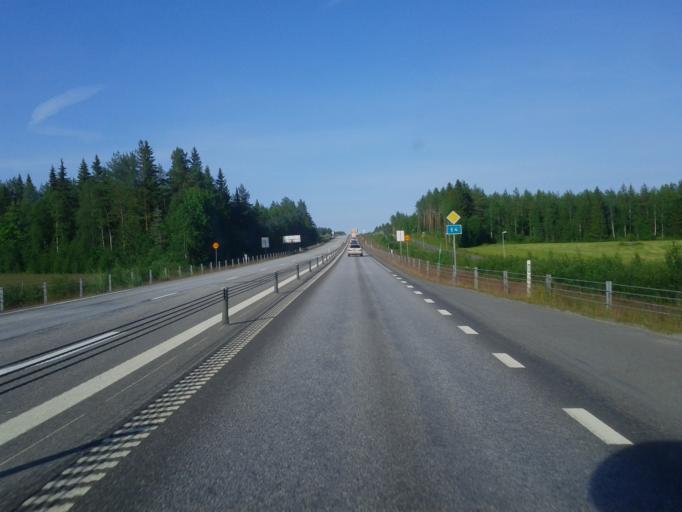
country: SE
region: Vaesterbotten
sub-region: Umea Kommun
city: Taftea
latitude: 63.8716
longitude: 20.4543
